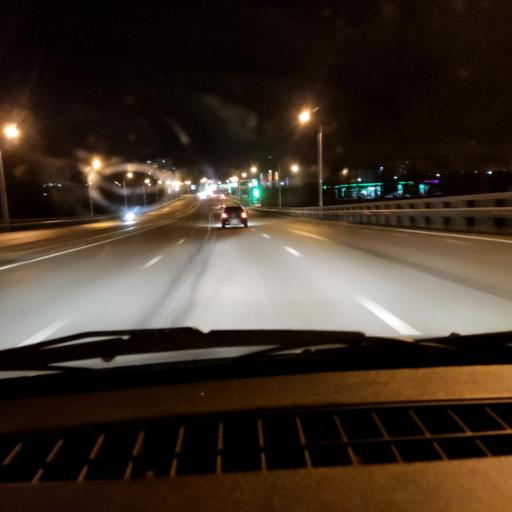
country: RU
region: Bashkortostan
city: Mikhaylovka
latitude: 54.7056
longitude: 55.8537
